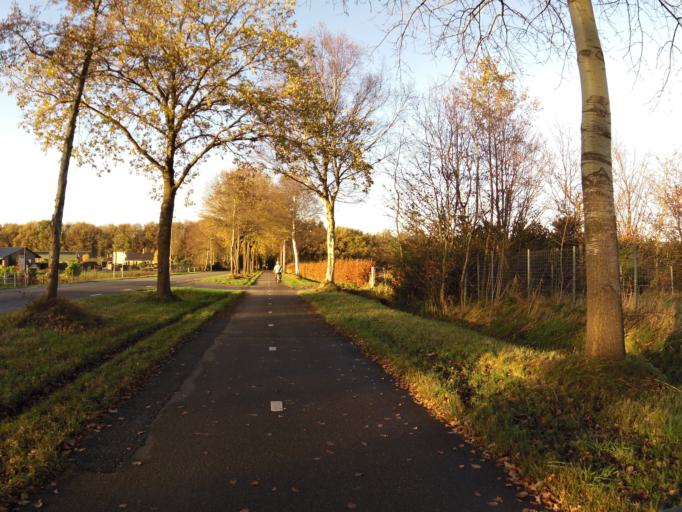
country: NL
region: North Brabant
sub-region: Gemeente Heusden
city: Heusden
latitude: 51.6635
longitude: 5.1454
